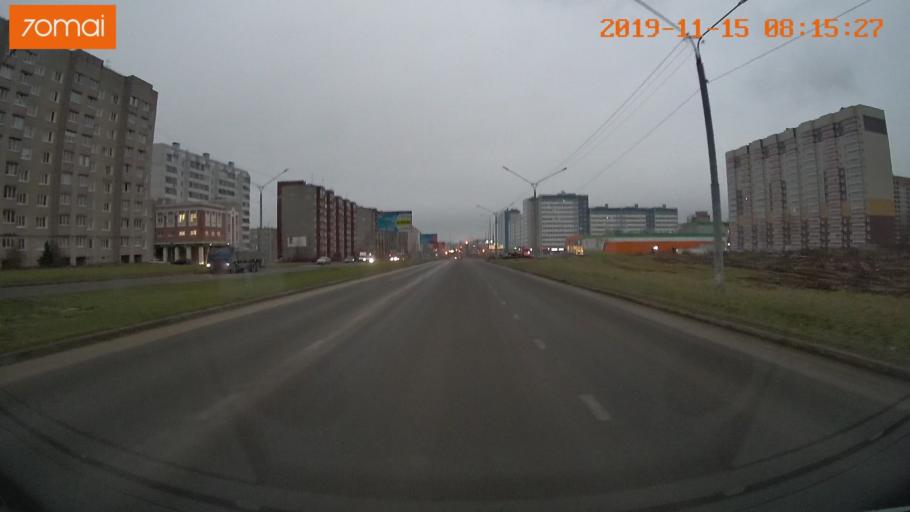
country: RU
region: Vologda
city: Cherepovets
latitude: 59.0824
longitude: 37.9222
